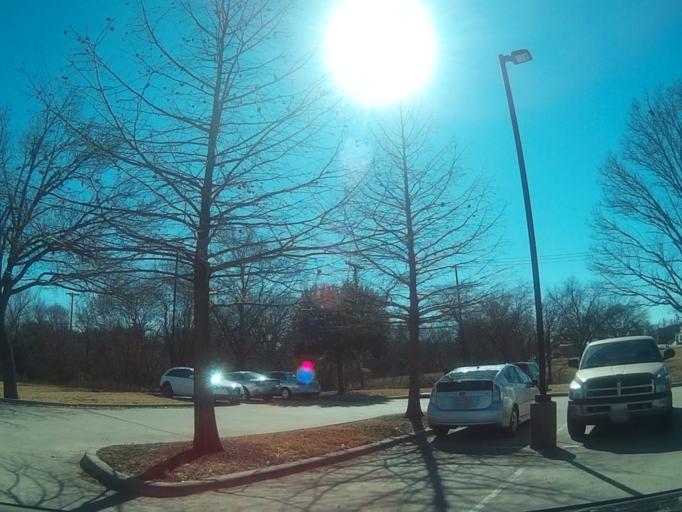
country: US
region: Texas
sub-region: Collin County
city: Allen
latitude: 33.1052
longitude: -96.6698
